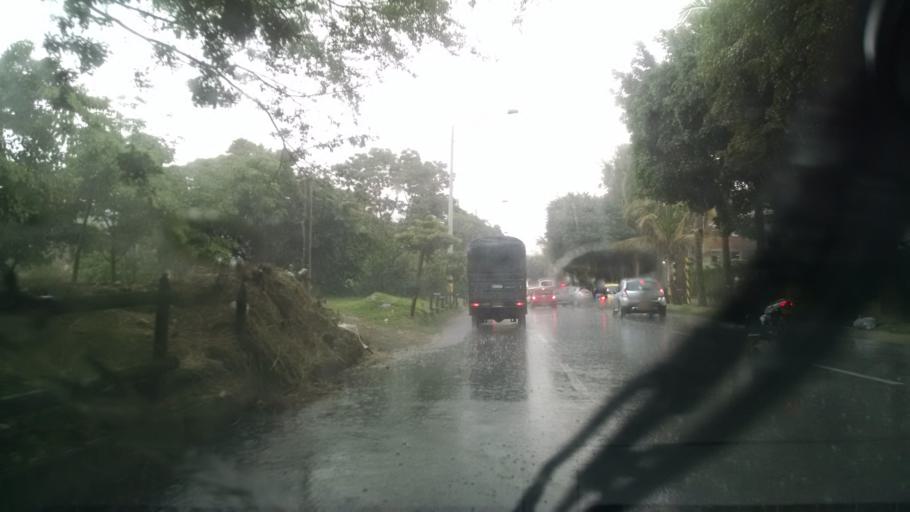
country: CO
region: Antioquia
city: Medellin
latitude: 6.2624
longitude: -75.5857
